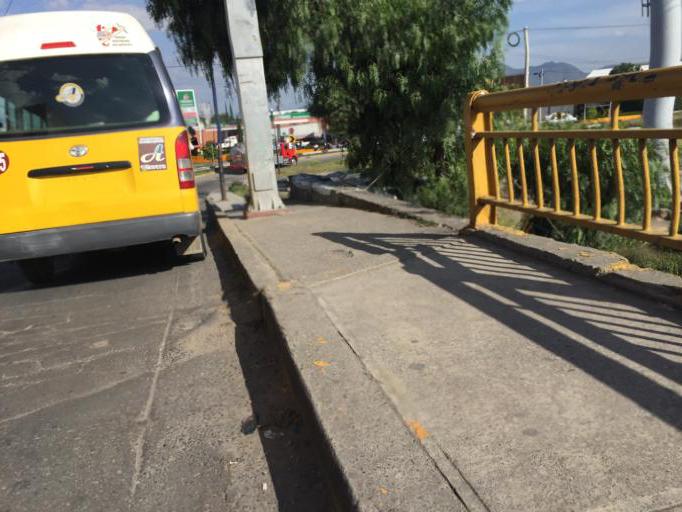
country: MX
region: Mexico
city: Cuautitlan
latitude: 19.6694
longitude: -99.1996
